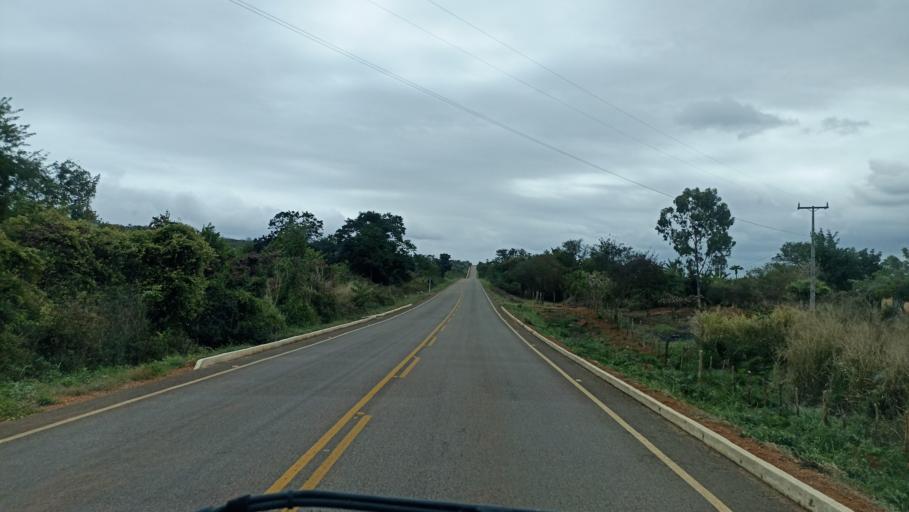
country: BR
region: Bahia
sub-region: Andarai
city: Vera Cruz
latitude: -13.0024
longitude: -40.9890
